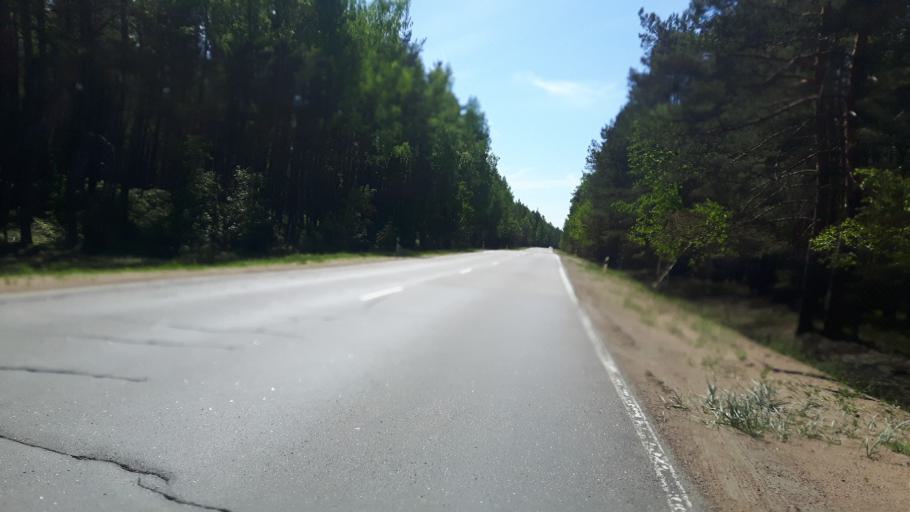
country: RU
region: Leningrad
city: Sista-Palkino
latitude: 59.7729
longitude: 28.8476
